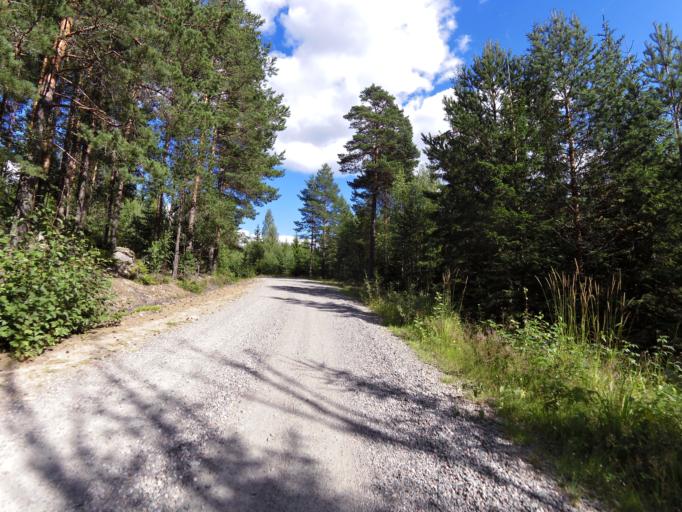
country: SE
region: Dalarna
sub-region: Faluns Kommun
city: Svardsjo
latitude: 60.6617
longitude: 15.8977
